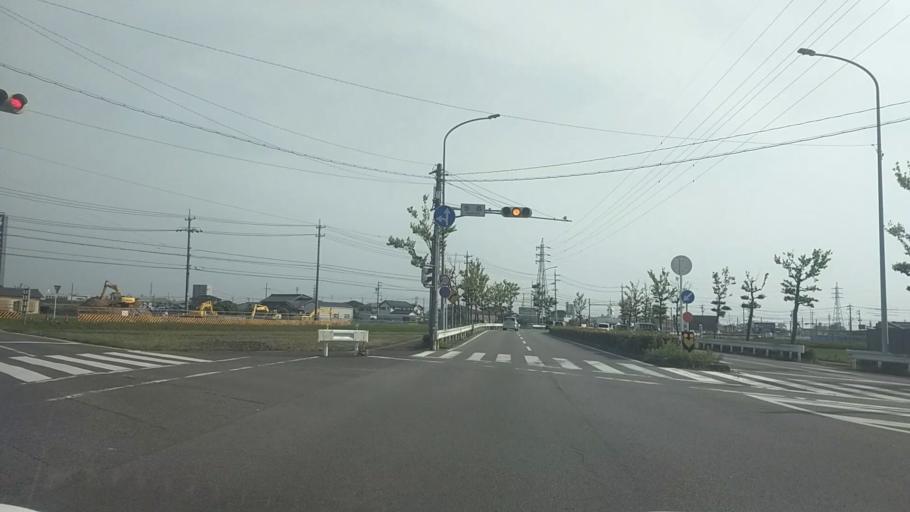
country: JP
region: Aichi
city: Anjo
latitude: 34.9675
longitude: 137.0732
